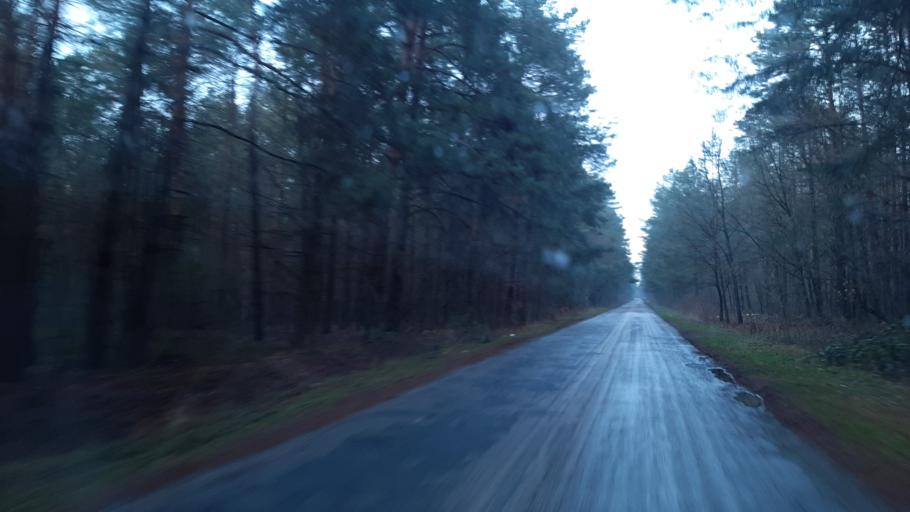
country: PL
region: Lublin Voivodeship
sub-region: Powiat lubartowski
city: Kamionka
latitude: 51.4835
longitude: 22.4745
